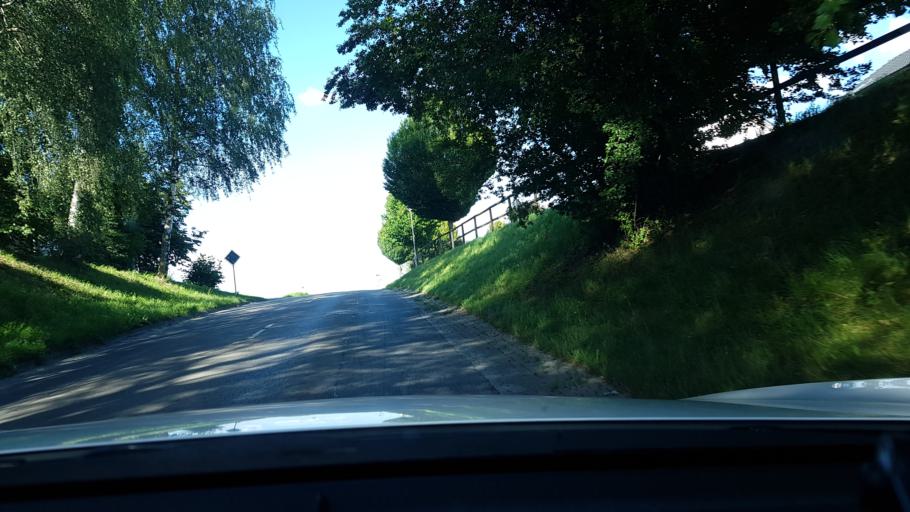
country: DE
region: Baden-Wuerttemberg
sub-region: Tuebingen Region
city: Schwendi
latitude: 48.1575
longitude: 9.9489
